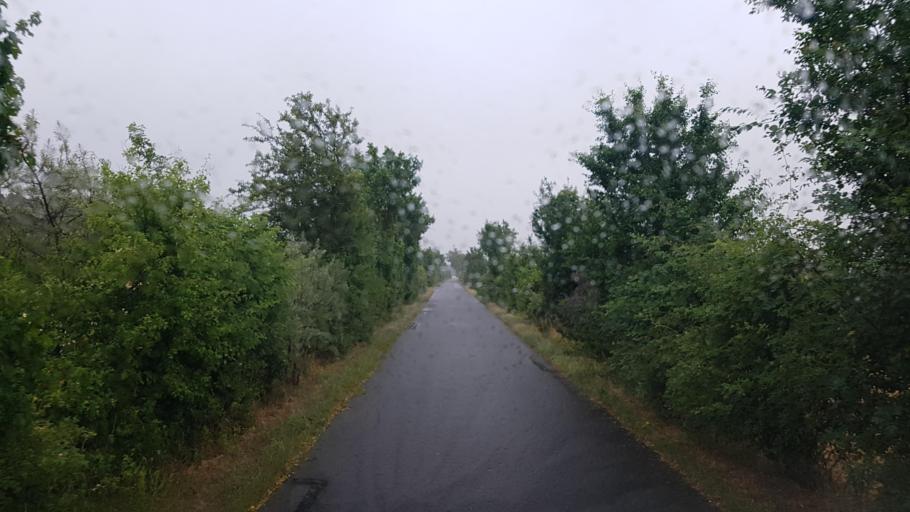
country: DE
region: Brandenburg
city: Muhlberg
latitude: 51.4637
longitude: 13.2991
